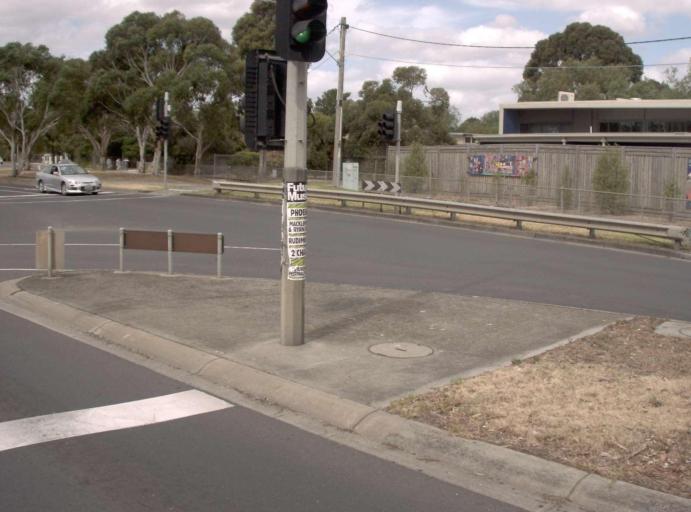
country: AU
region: Victoria
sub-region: Casey
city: Doveton
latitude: -37.9874
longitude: 145.2199
